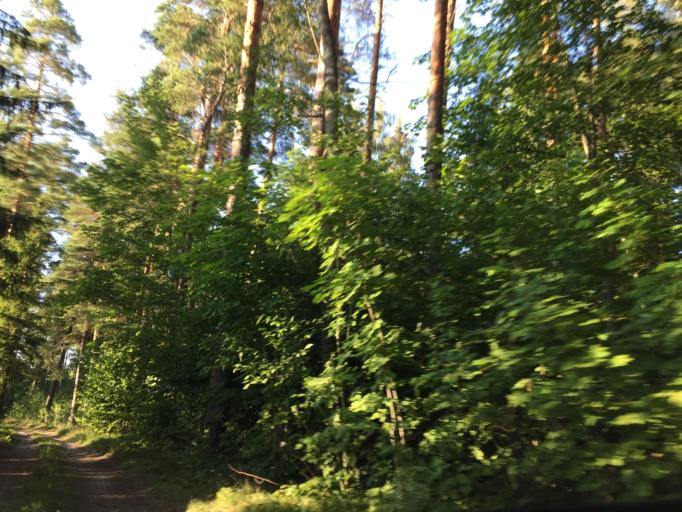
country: LV
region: Talsu Rajons
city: Stende
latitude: 57.1589
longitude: 22.3039
